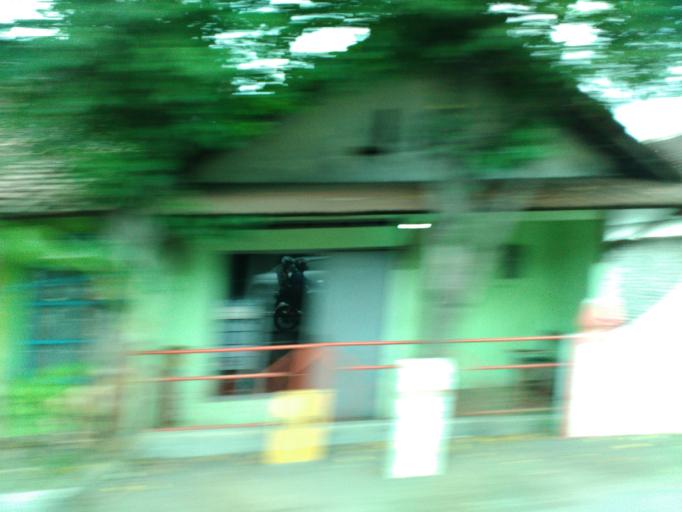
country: ID
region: Central Java
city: Gatak
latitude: -7.5838
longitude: 110.7135
